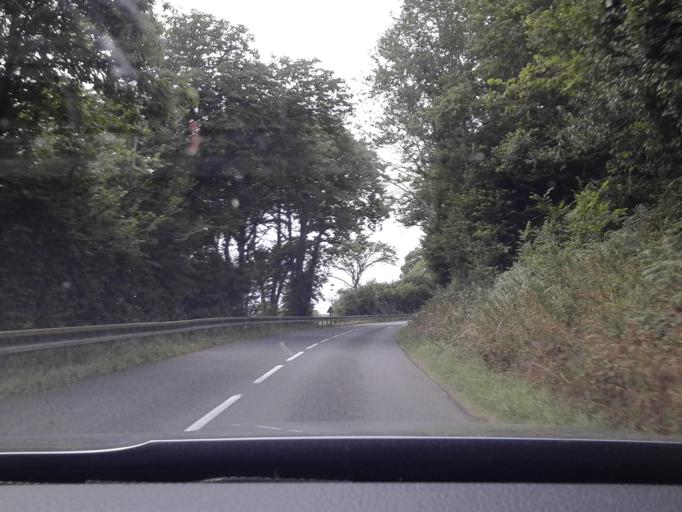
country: FR
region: Lower Normandy
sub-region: Departement de la Manche
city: Beaumont-Hague
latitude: 49.6720
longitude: -1.8263
